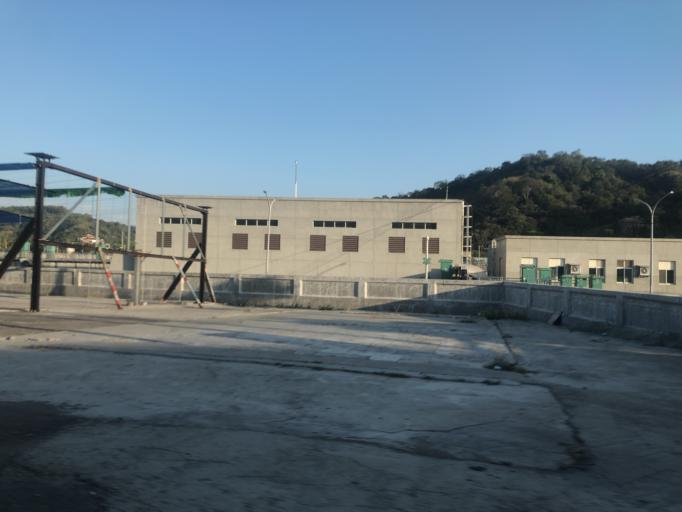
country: TW
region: Taiwan
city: Fengyuan
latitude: 24.2783
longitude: 120.7673
